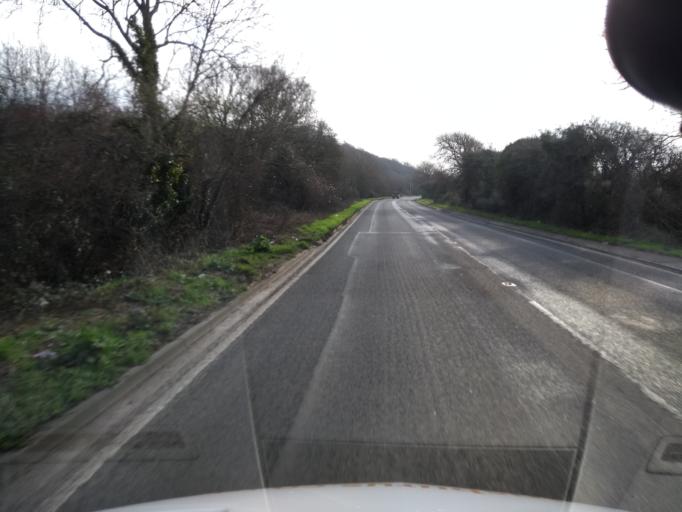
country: GB
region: England
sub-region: North Somerset
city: Bleadon
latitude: 51.3123
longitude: -2.9649
